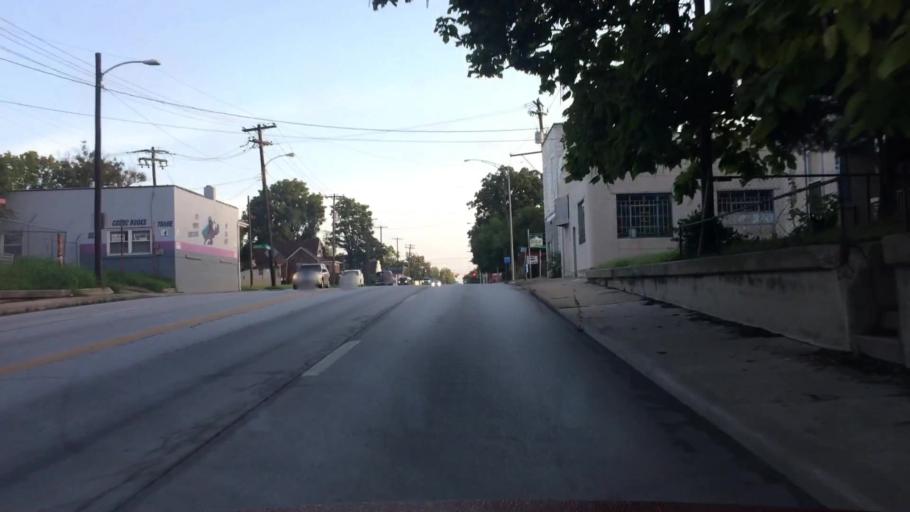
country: US
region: Missouri
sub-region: Greene County
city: Springfield
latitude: 37.2327
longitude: -93.2751
